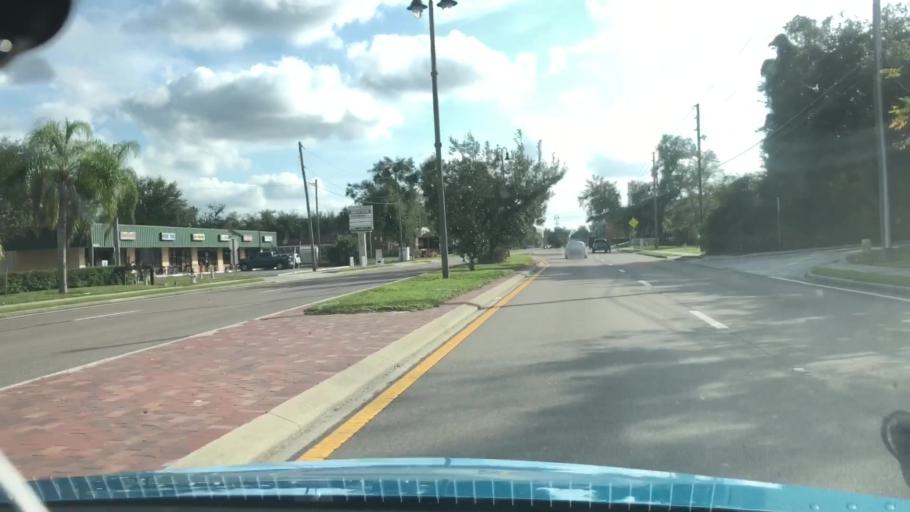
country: US
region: Florida
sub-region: Seminole County
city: Longwood
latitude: 28.6900
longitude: -81.3460
